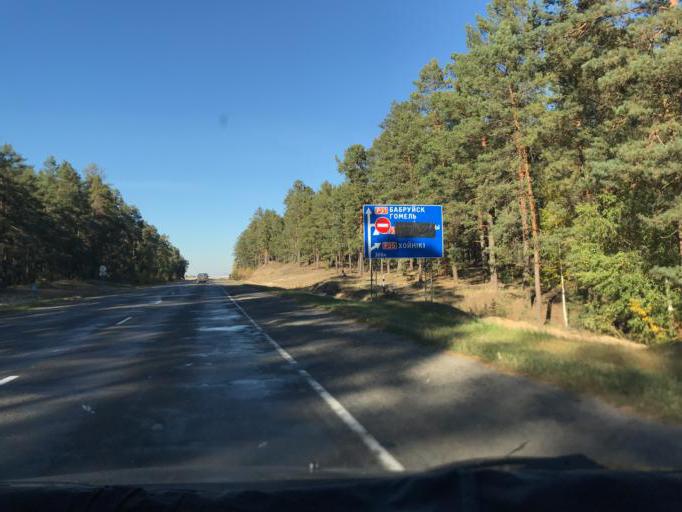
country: BY
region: Gomel
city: Kalinkavichy
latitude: 52.0660
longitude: 29.3611
